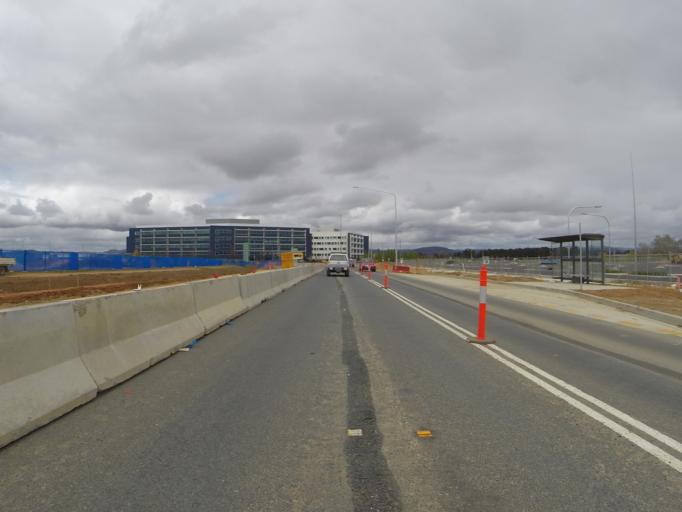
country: AU
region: Australian Capital Territory
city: Canberra
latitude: -35.2961
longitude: 149.1879
